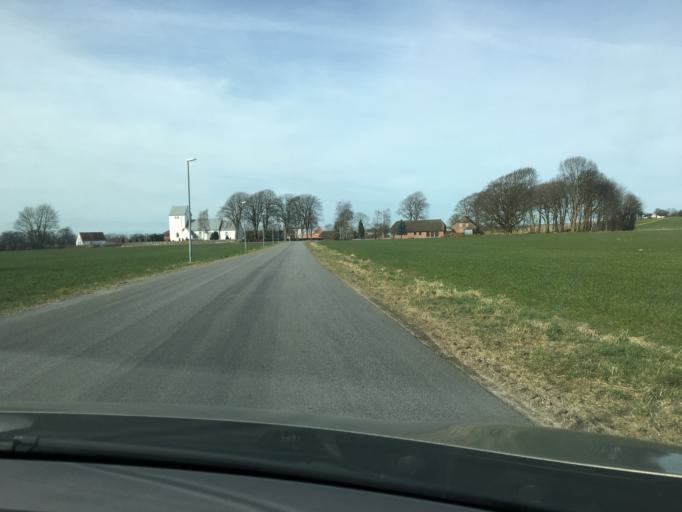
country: DK
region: Central Jutland
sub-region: Hedensted Kommune
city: Hedensted
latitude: 55.7386
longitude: 9.6597
